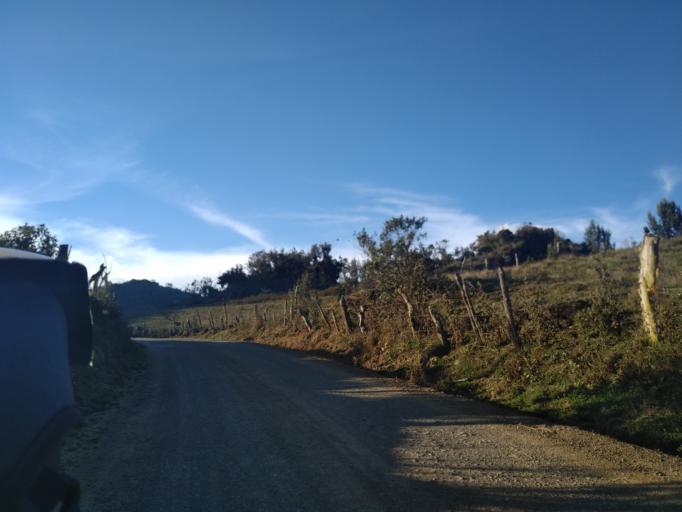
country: PE
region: Amazonas
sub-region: Provincia de Chachapoyas
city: Montevideo
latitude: -6.7140
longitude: -77.8657
